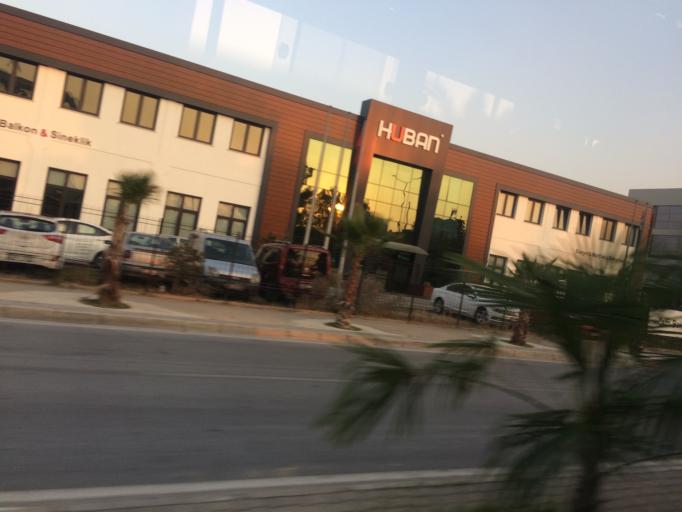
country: TR
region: Izmir
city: Karsiyaka
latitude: 38.5004
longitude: 27.0372
